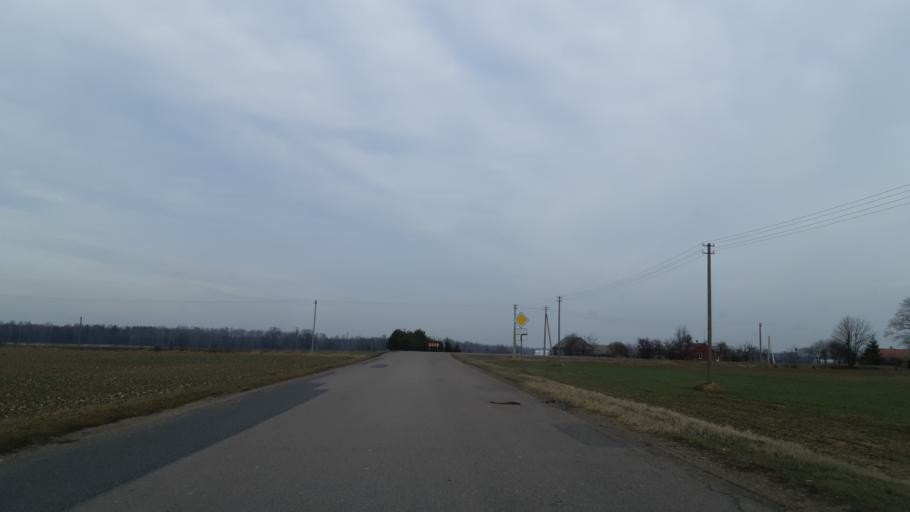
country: LT
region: Marijampoles apskritis
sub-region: Marijampole Municipality
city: Marijampole
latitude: 54.7171
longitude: 23.3223
